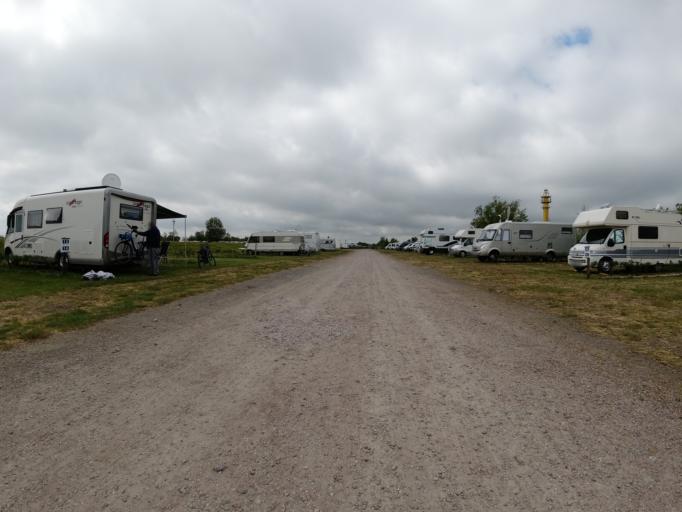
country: DE
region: Lower Saxony
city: Schillig
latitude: 53.7010
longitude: 8.0243
